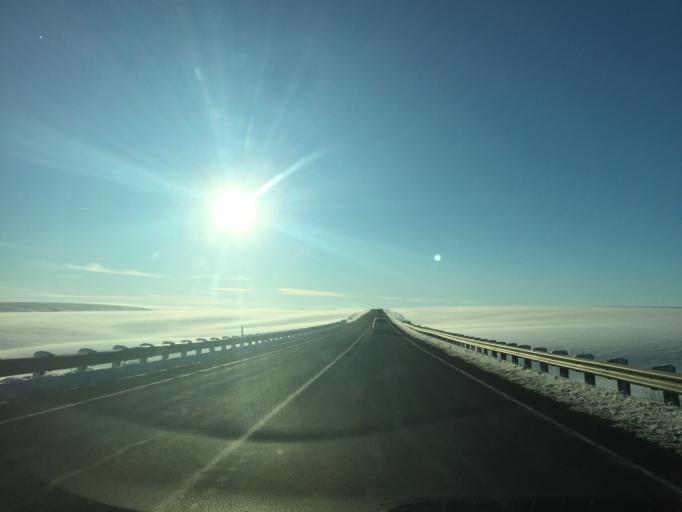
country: US
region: Washington
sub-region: Okanogan County
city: Coulee Dam
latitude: 47.6988
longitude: -118.9585
